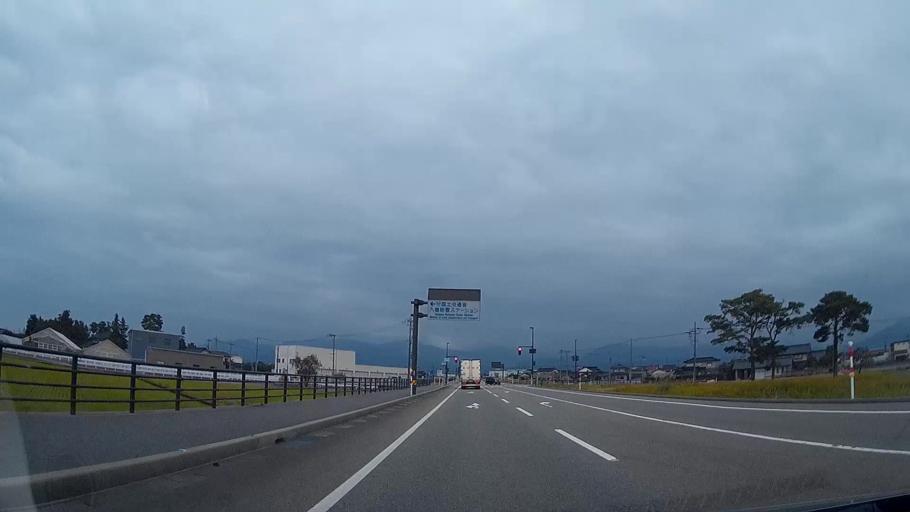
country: JP
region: Toyama
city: Nyuzen
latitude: 36.9270
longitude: 137.4864
